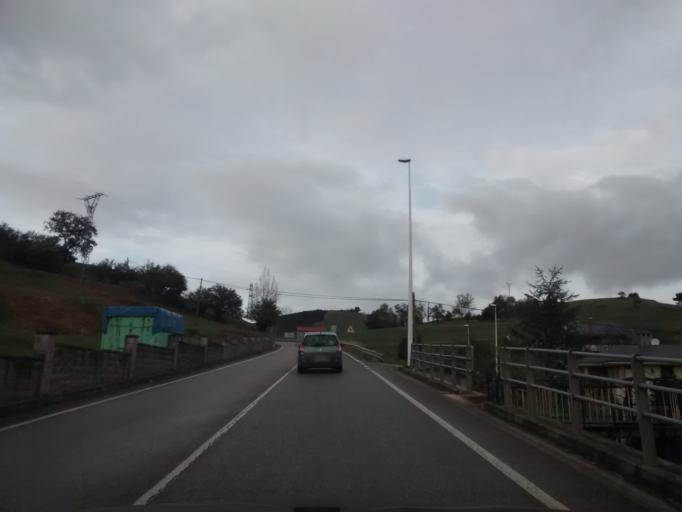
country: ES
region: Cantabria
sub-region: Provincia de Cantabria
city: Lierganes
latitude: 43.3484
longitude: -3.7467
